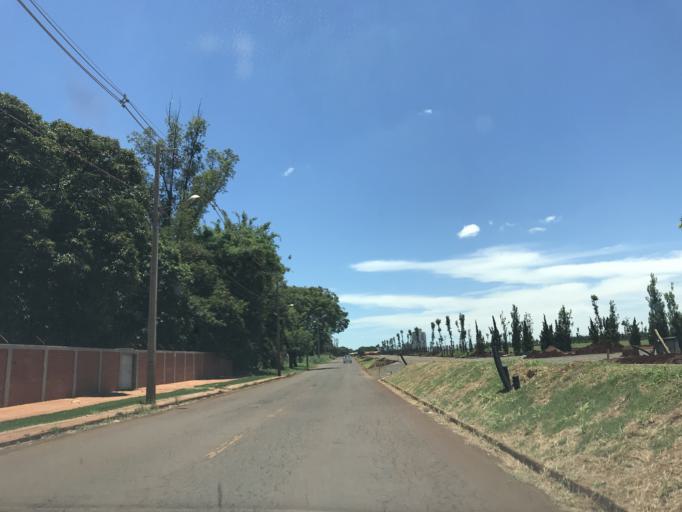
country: BR
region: Parana
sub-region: Sarandi
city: Sarandi
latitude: -23.4398
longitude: -51.9013
